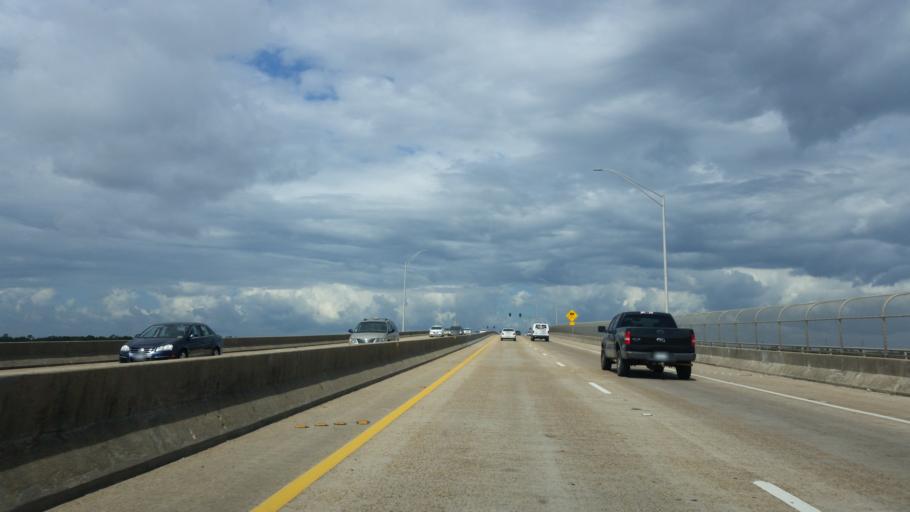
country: US
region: Mississippi
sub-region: Harrison County
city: D'Iberville
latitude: 30.4186
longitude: -88.8942
